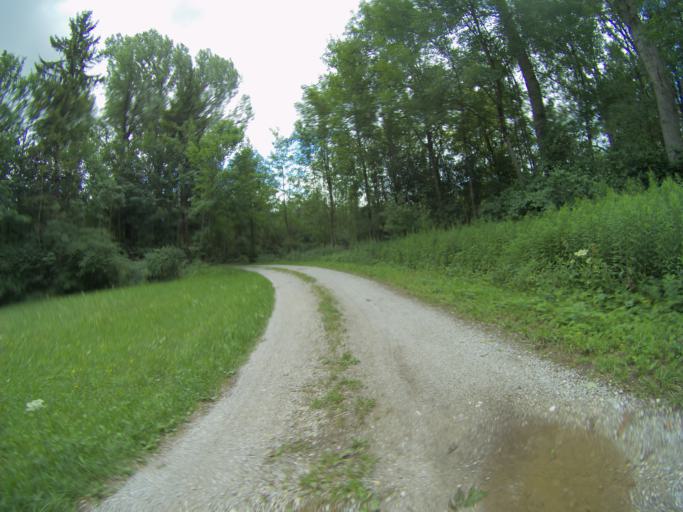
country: DE
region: Bavaria
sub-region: Upper Bavaria
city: Freising
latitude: 48.3787
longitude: 11.7405
